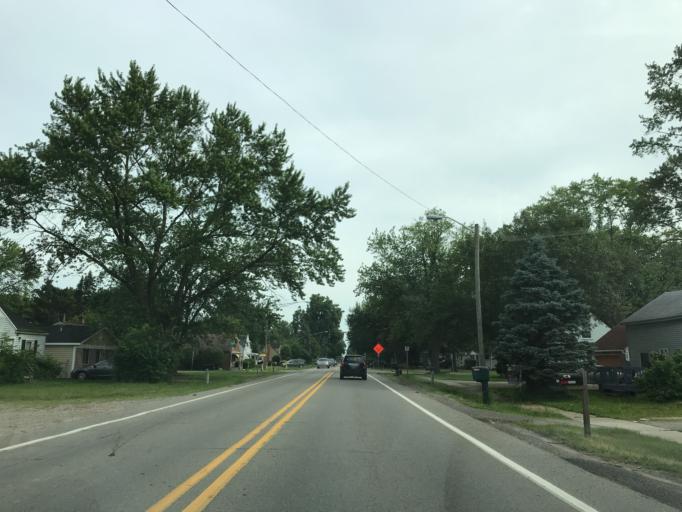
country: US
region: Michigan
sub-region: Wayne County
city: Redford
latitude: 42.4355
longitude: -83.3166
